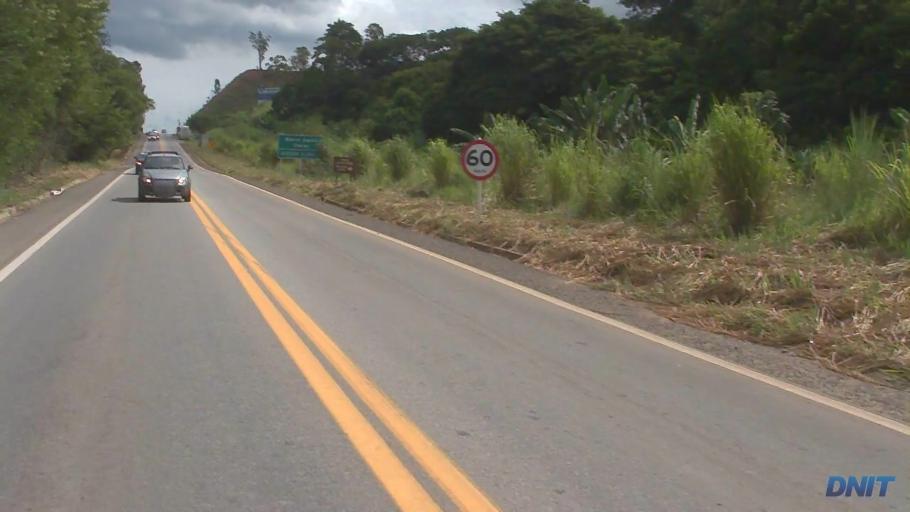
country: BR
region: Minas Gerais
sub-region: Ipatinga
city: Ipatinga
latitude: -19.4426
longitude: -42.5125
